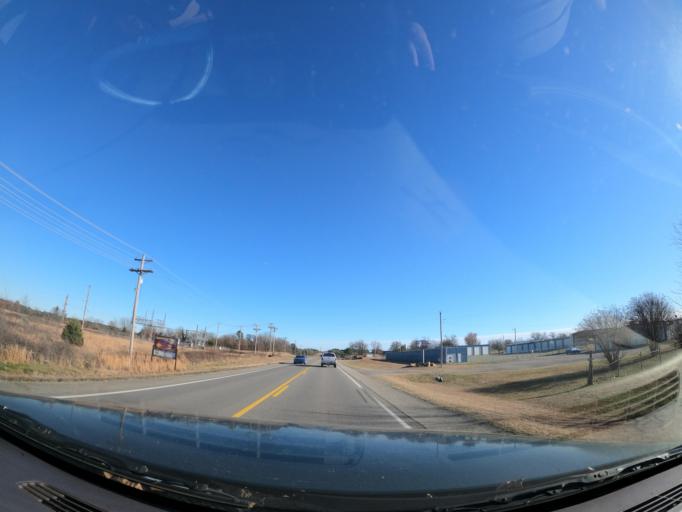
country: US
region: Oklahoma
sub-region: Pittsburg County
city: Longtown
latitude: 35.2351
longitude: -95.4633
